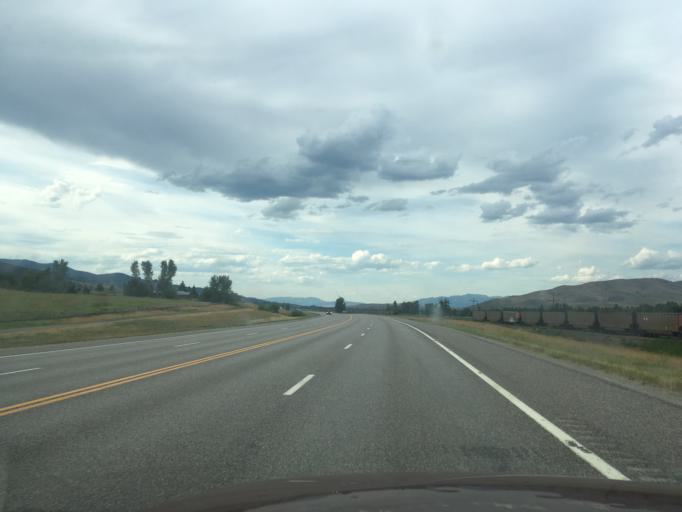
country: US
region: Montana
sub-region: Missoula County
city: Lolo
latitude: 46.6955
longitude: -114.0738
